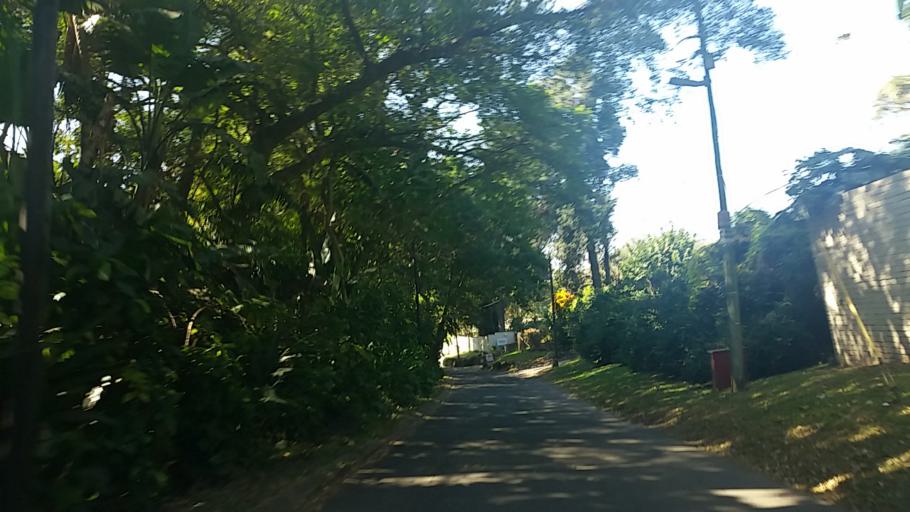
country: ZA
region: KwaZulu-Natal
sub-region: eThekwini Metropolitan Municipality
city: Berea
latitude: -29.8403
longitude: 30.9018
